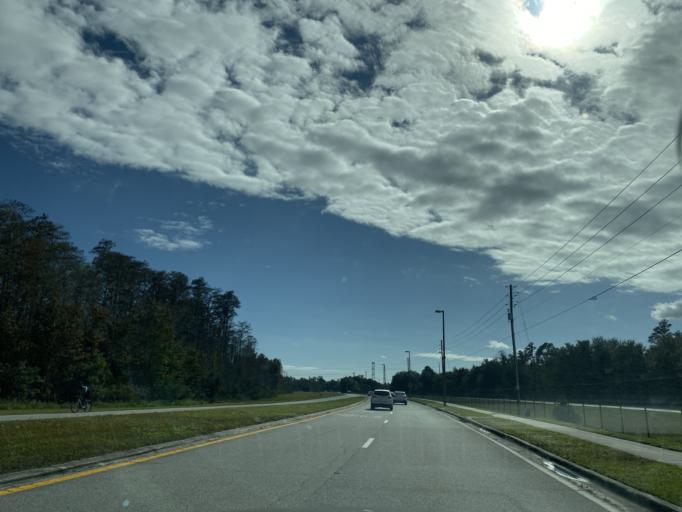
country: US
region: Florida
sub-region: Orange County
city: Azalea Park
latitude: 28.5076
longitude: -81.2566
